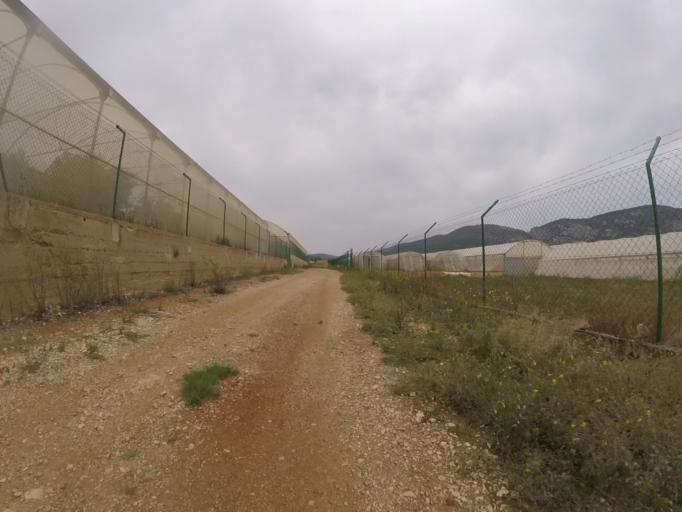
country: ES
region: Valencia
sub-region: Provincia de Castello
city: Alcala de Xivert
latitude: 40.2811
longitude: 0.2550
